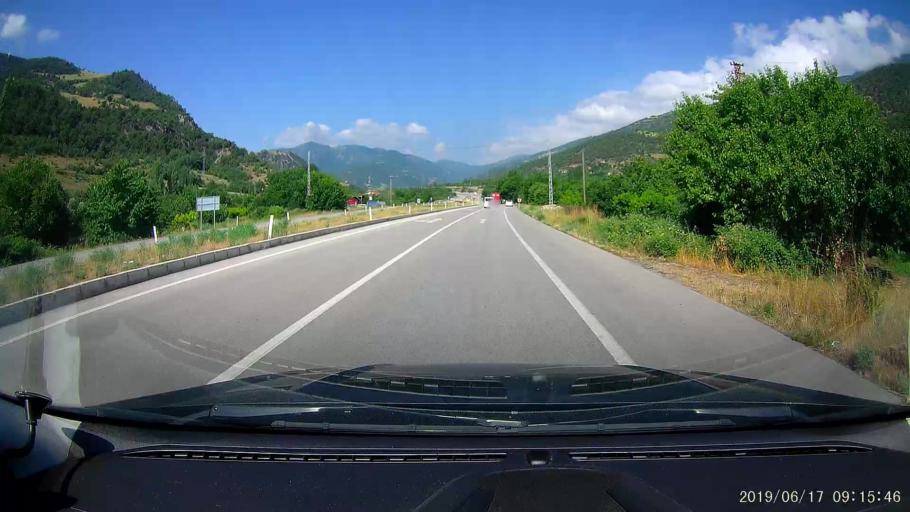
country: TR
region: Amasya
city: Akdag
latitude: 40.7465
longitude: 36.0281
